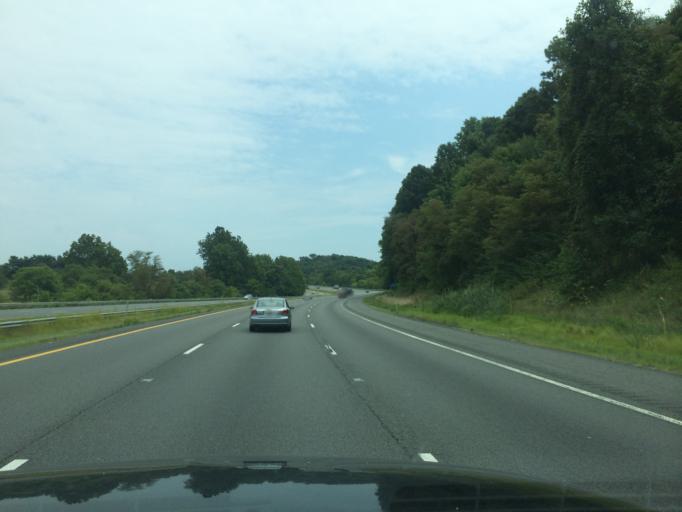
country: US
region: Maryland
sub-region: Carroll County
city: Mount Airy
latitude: 39.3701
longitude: -77.2039
